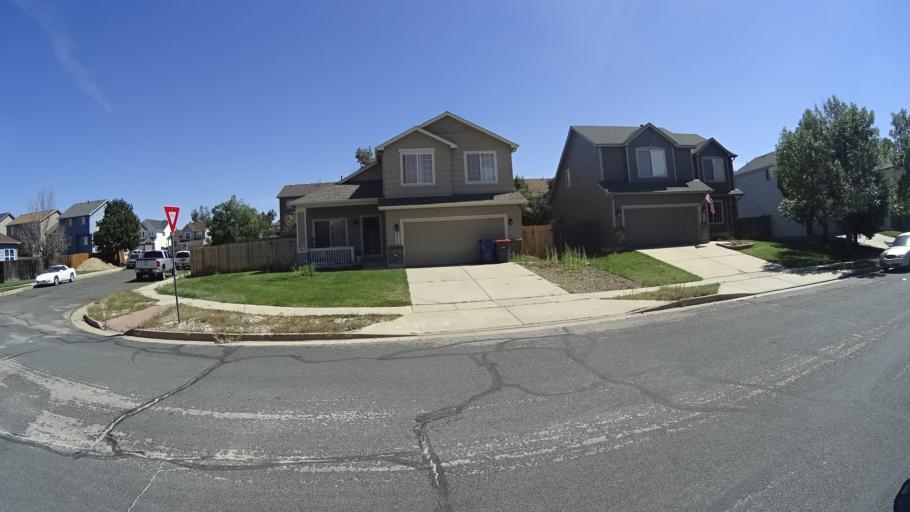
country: US
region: Colorado
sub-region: El Paso County
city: Black Forest
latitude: 38.9499
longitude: -104.7593
